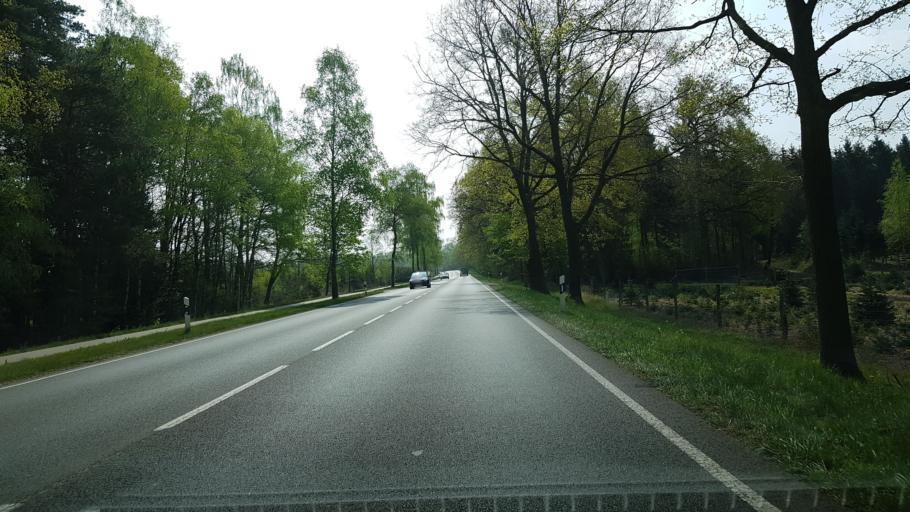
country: DE
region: Lower Saxony
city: Soltau
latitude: 52.9630
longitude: 9.8576
